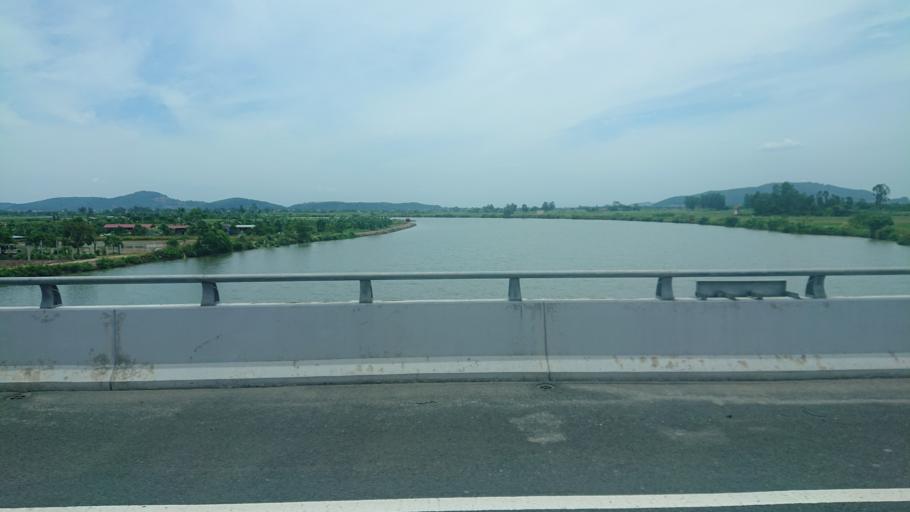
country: VN
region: Hai Phong
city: An Lao
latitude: 20.7767
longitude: 106.5760
